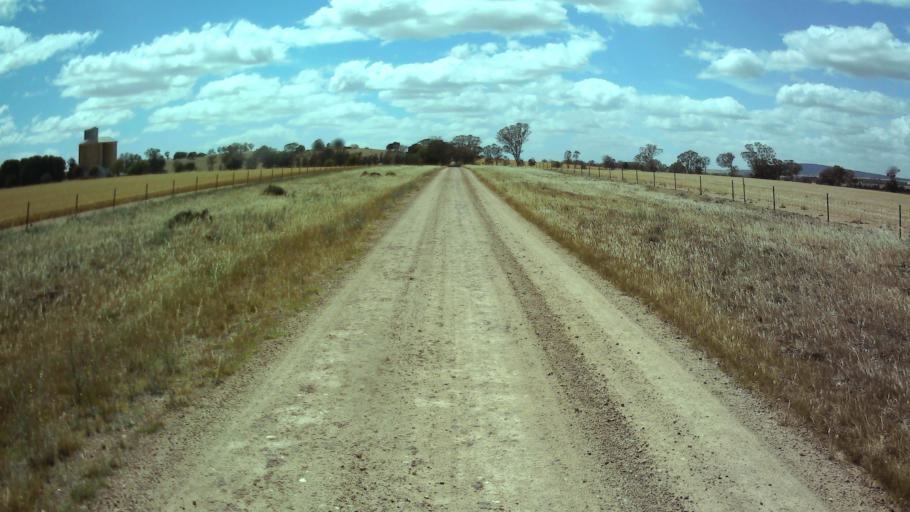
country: AU
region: New South Wales
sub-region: Weddin
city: Grenfell
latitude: -33.9914
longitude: 148.3341
